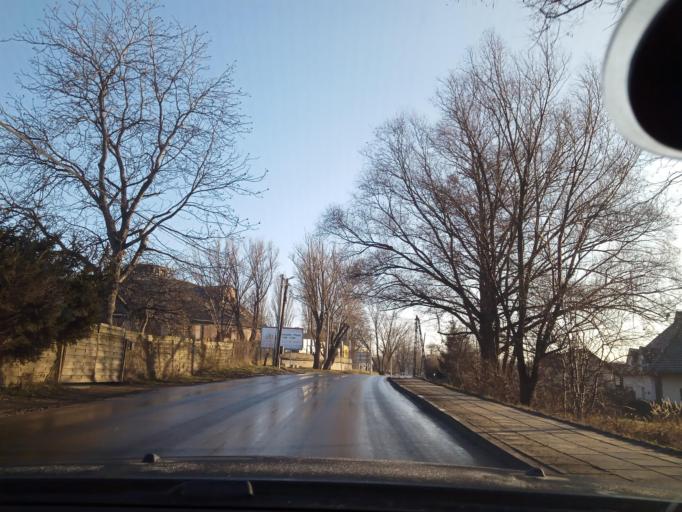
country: PL
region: Lesser Poland Voivodeship
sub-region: Powiat krakowski
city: Michalowice
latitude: 50.1060
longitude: 20.0405
